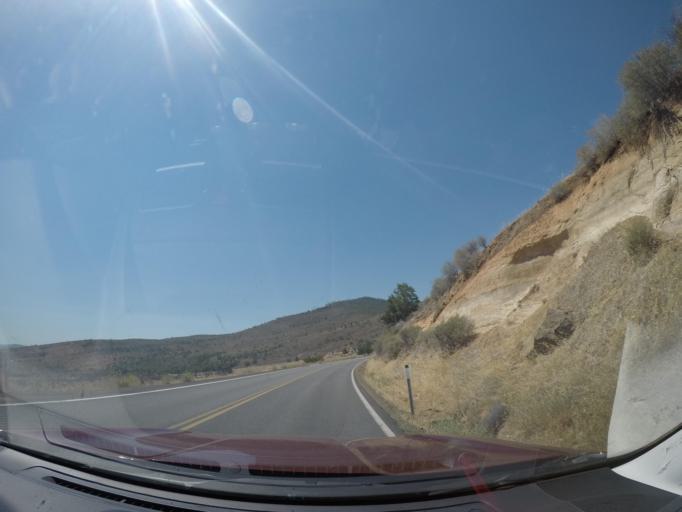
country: US
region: California
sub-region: Shasta County
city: Burney
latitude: 40.9988
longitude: -121.4994
